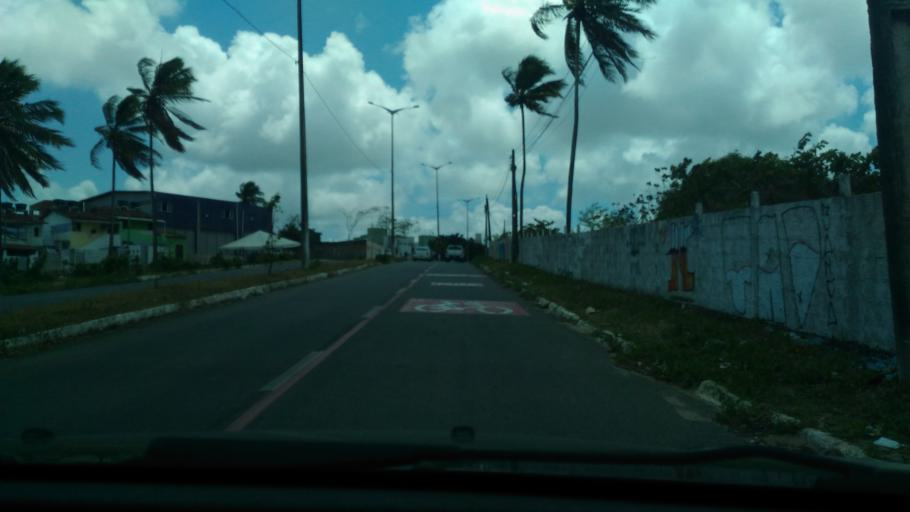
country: BR
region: Paraiba
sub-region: Joao Pessoa
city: Joao Pessoa
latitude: -7.1435
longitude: -34.8299
